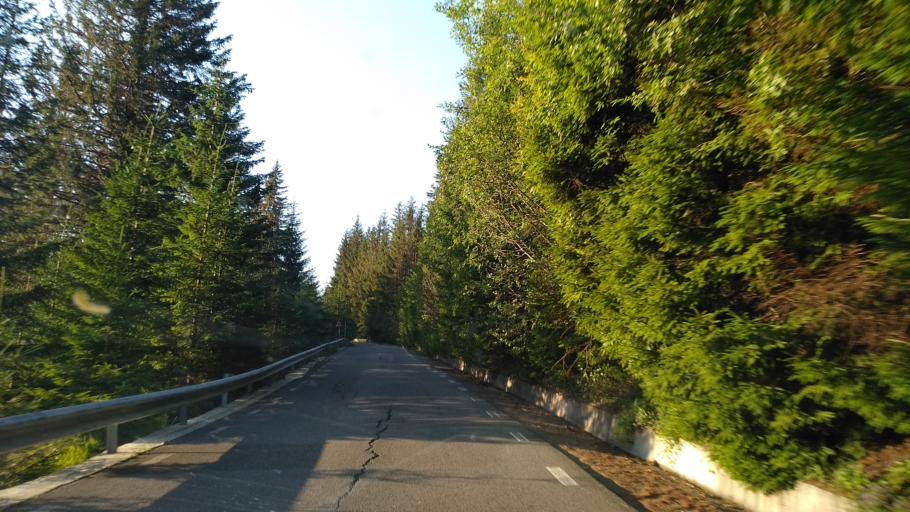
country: RO
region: Prahova
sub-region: Oras Sinaia
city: Sinaia
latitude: 45.3228
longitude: 25.4827
